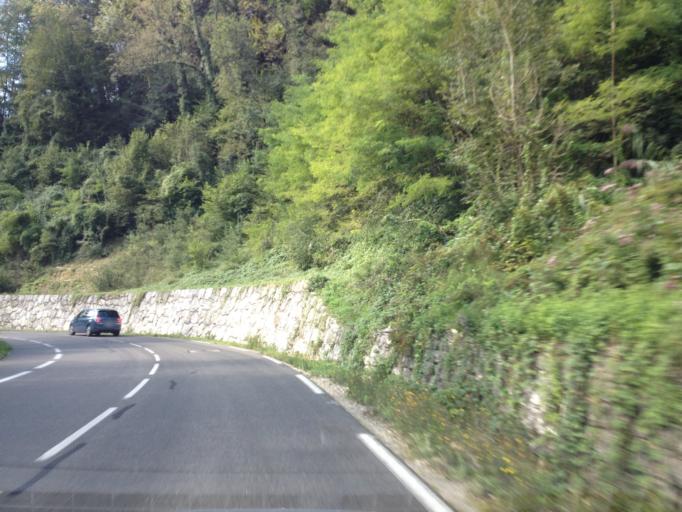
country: FR
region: Rhone-Alpes
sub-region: Departement de la Savoie
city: Gresy-sur-Aix
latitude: 45.7381
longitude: 5.9683
